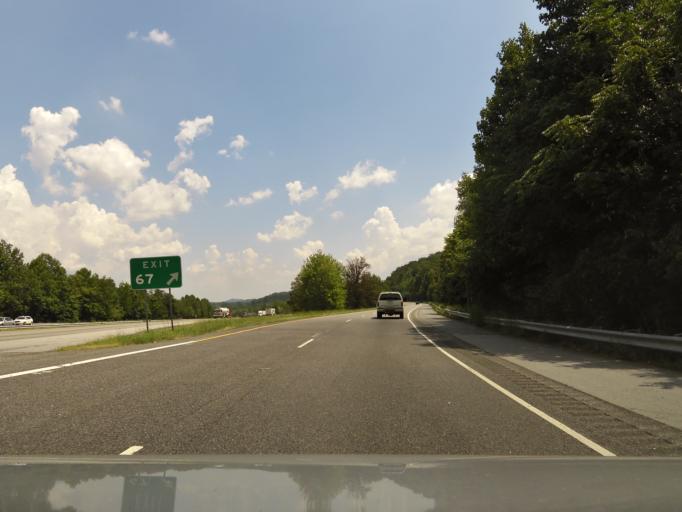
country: US
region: North Carolina
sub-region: Polk County
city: Columbus
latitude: 35.2530
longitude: -82.2177
